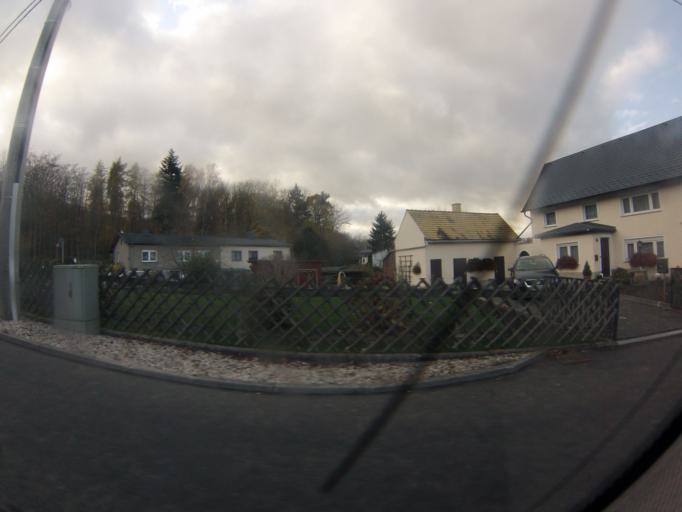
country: DE
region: Thuringia
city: Nobdenitz
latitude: 50.8727
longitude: 12.2828
